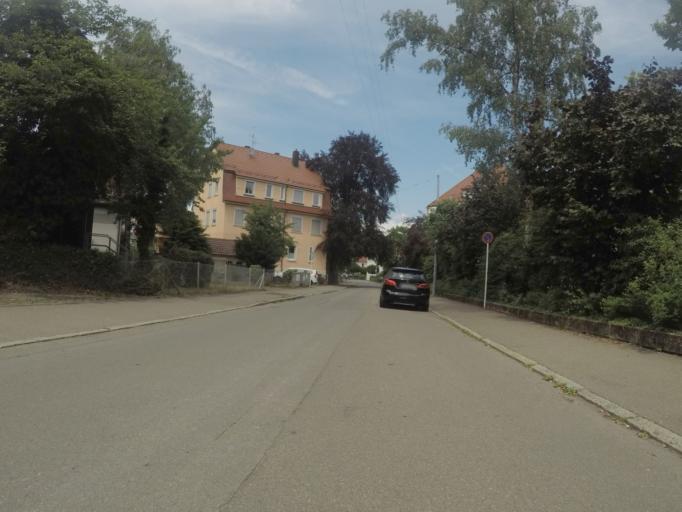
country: DE
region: Baden-Wuerttemberg
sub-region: Tuebingen Region
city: Reutlingen
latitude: 48.4866
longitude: 9.2108
